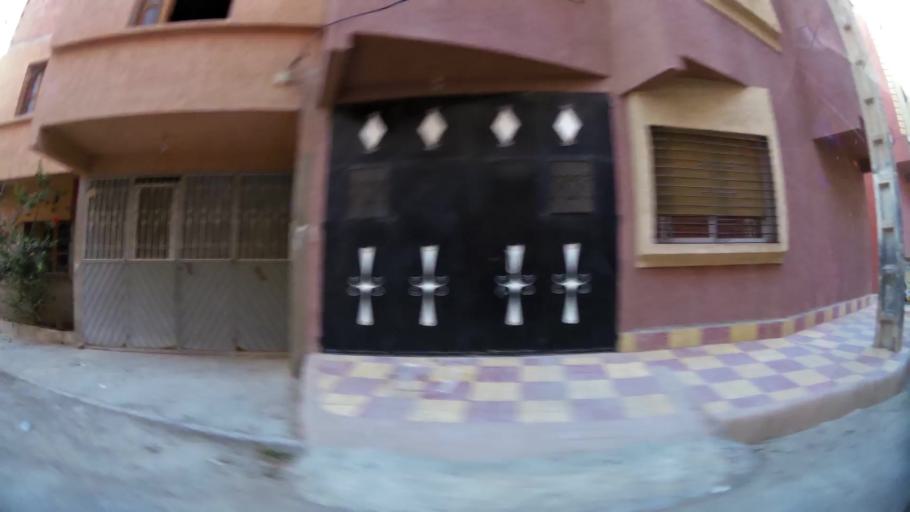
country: MA
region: Oriental
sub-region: Berkane-Taourirt
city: Berkane
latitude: 34.9270
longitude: -2.3395
